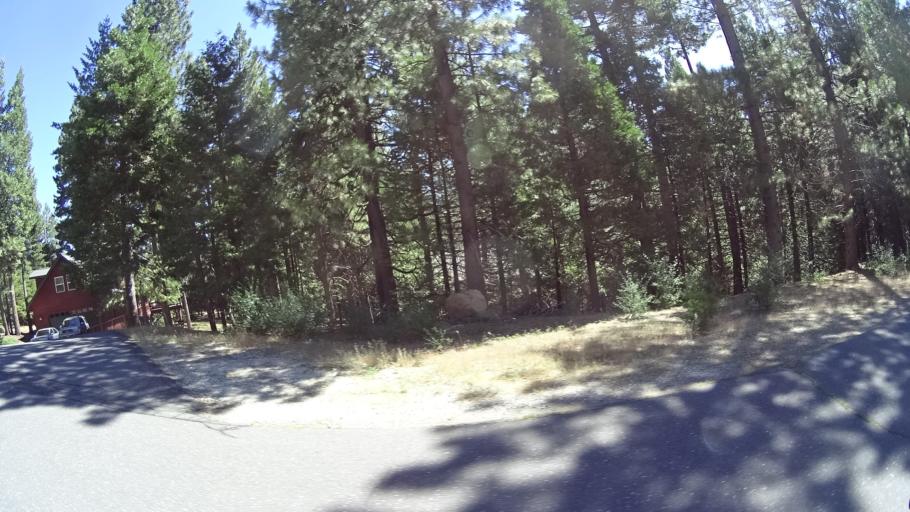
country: US
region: California
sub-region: Calaveras County
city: Arnold
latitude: 38.2868
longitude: -120.2845
